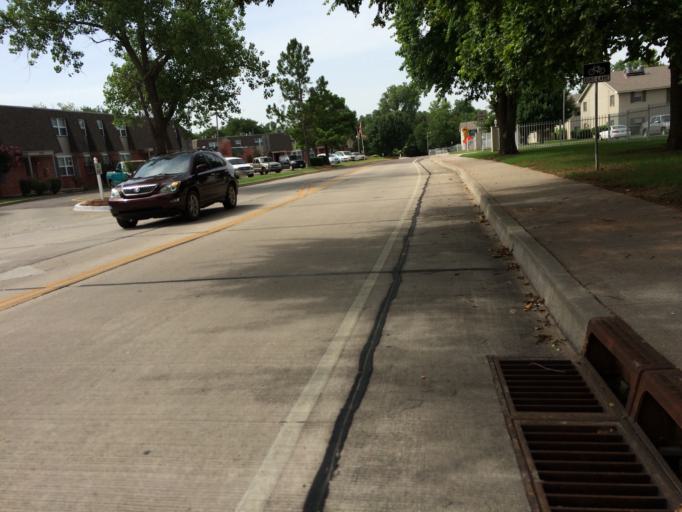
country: US
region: Oklahoma
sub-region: Cleveland County
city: Norman
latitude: 35.2038
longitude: -97.4139
